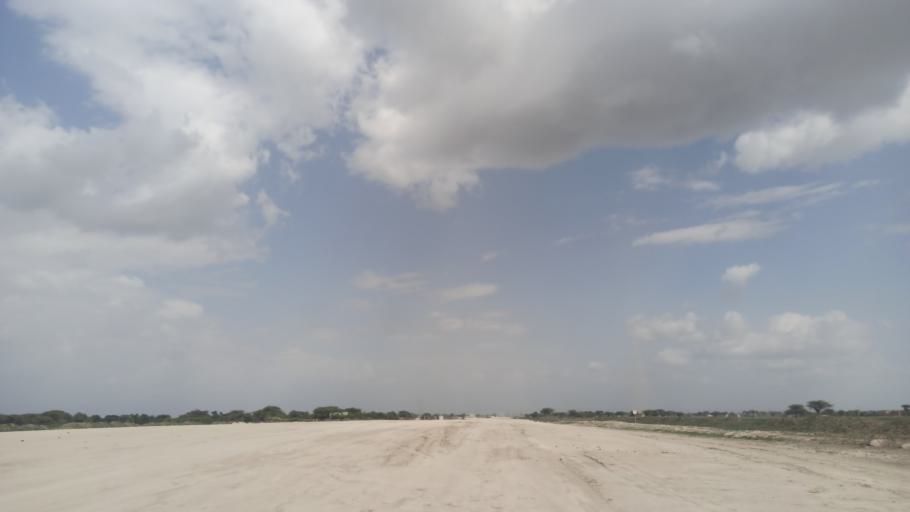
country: ET
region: Oromiya
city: Ziway
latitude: 7.7344
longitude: 38.6233
